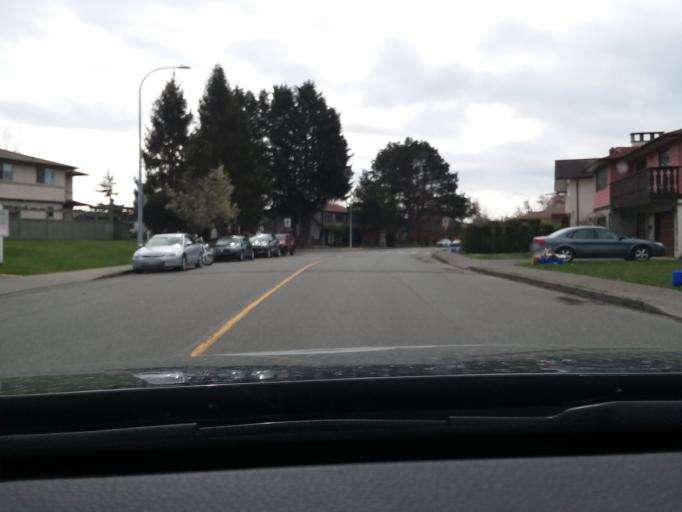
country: CA
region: British Columbia
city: Oak Bay
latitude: 48.4737
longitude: -123.3255
